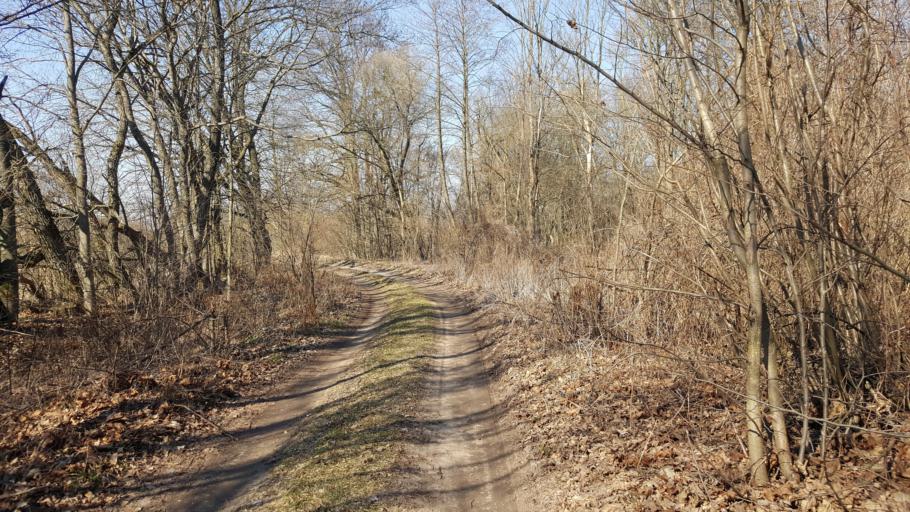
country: BY
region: Brest
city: Kamyanyets
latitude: 52.3613
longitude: 23.7472
